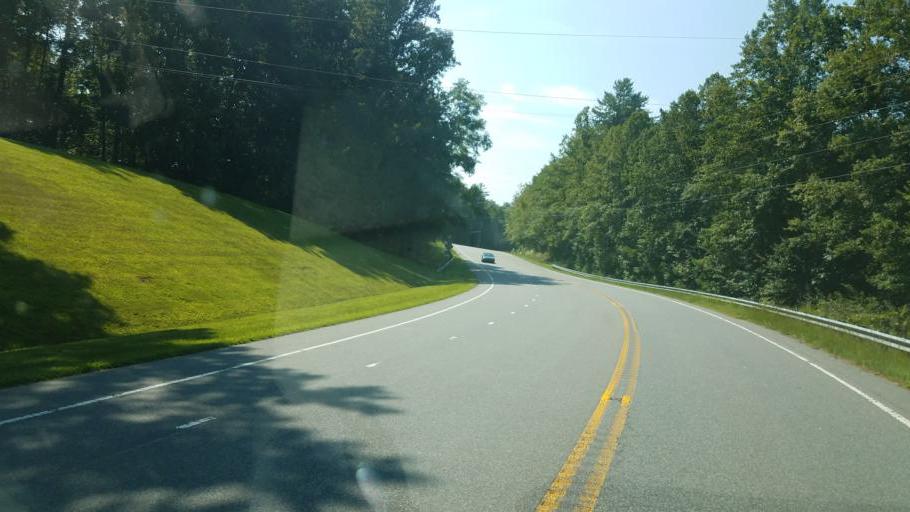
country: US
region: North Carolina
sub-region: Burke County
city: Glen Alpine
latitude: 35.8786
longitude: -81.7949
